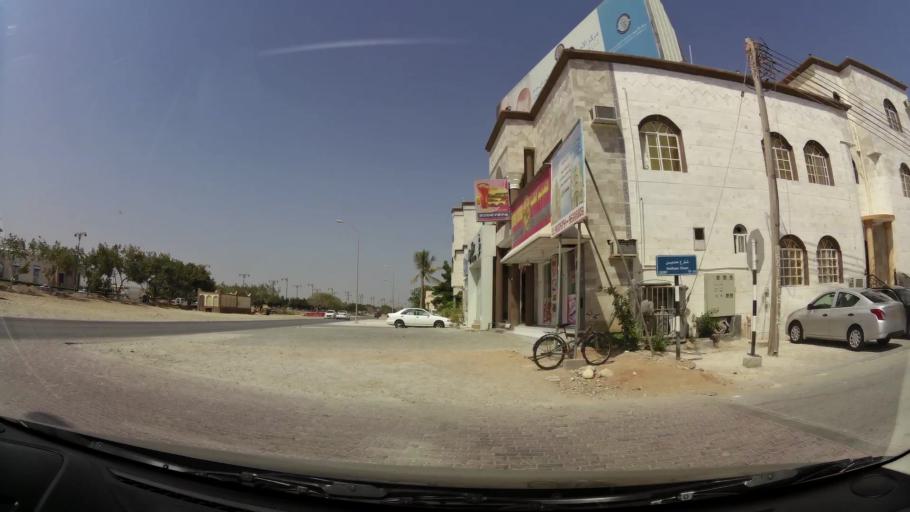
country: OM
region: Zufar
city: Salalah
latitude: 17.0209
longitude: 54.0664
